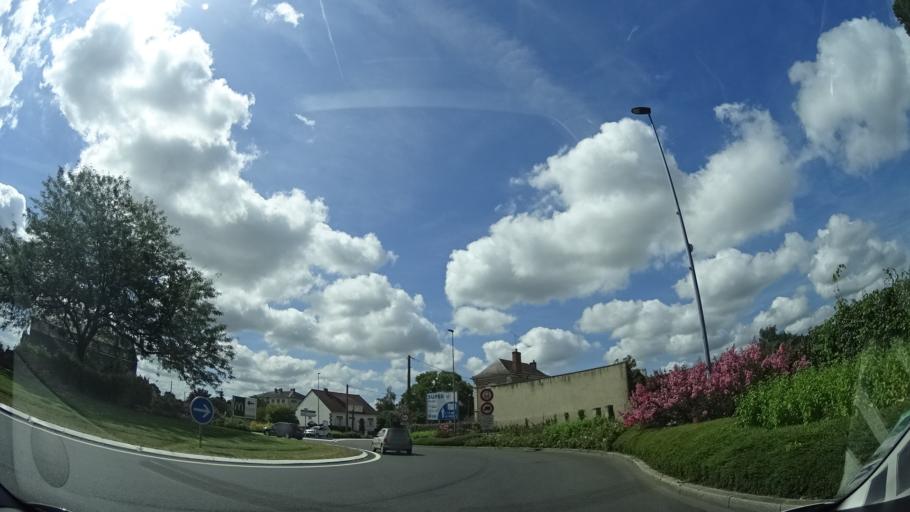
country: FR
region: Pays de la Loire
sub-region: Departement de la Sarthe
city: La Fleche
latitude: 47.6985
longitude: -0.0880
